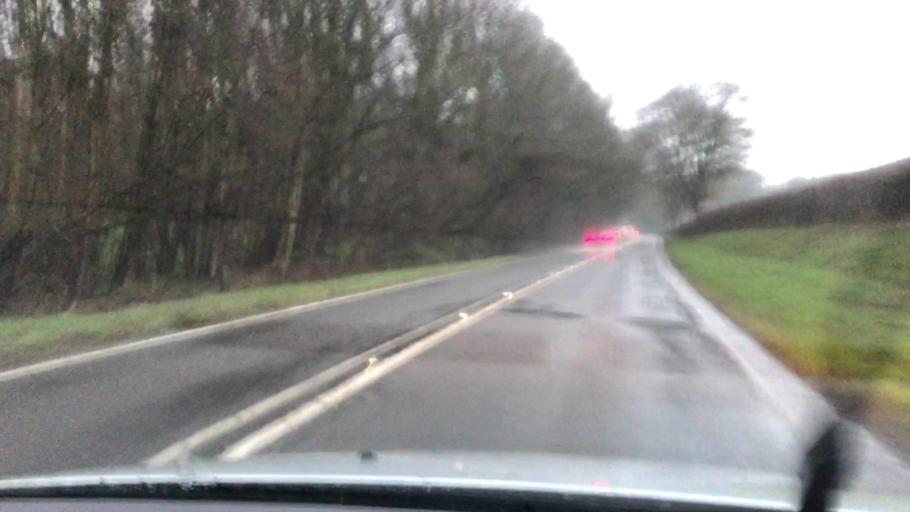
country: GB
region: England
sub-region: Hampshire
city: Alton
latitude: 51.1800
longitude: -0.9887
